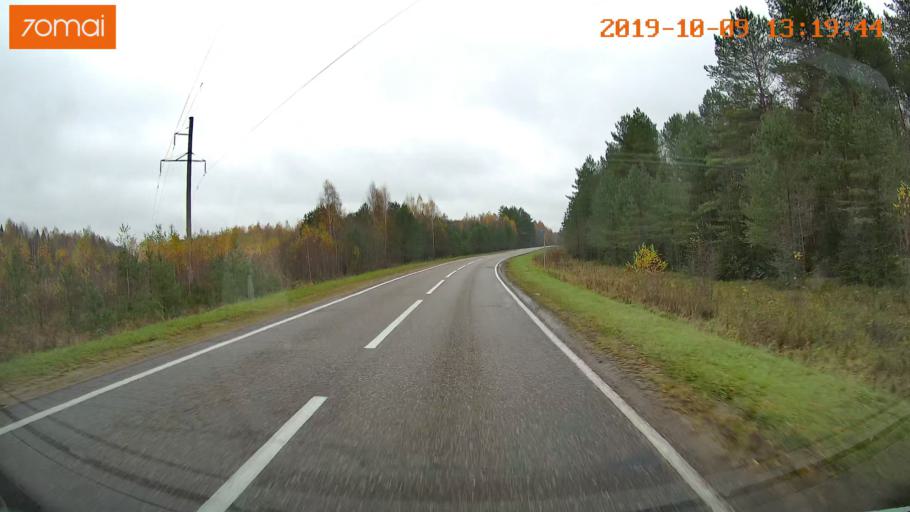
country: RU
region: Jaroslavl
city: Lyubim
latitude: 58.3479
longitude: 40.8193
